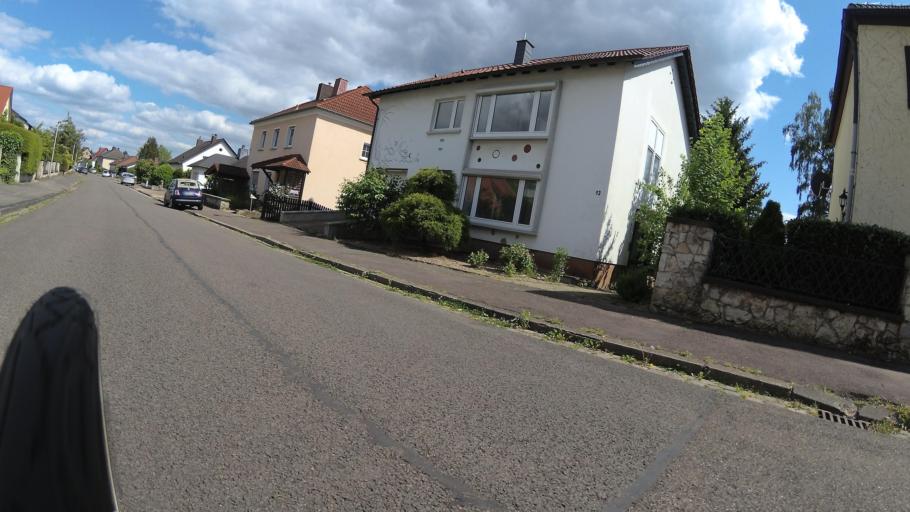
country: DE
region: Saarland
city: Volklingen
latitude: 49.2617
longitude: 6.8600
